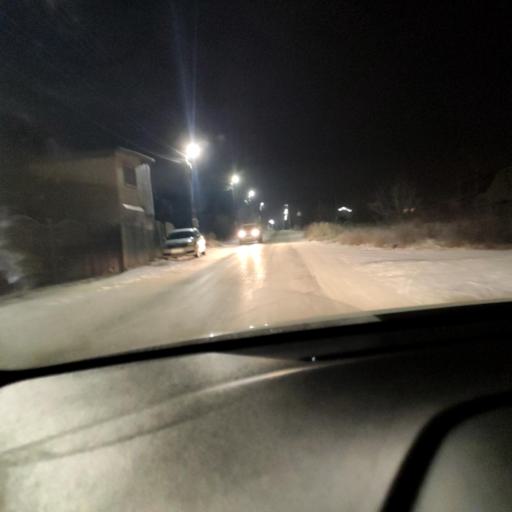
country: RU
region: Tatarstan
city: Staroye Arakchino
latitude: 55.8843
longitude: 49.0396
